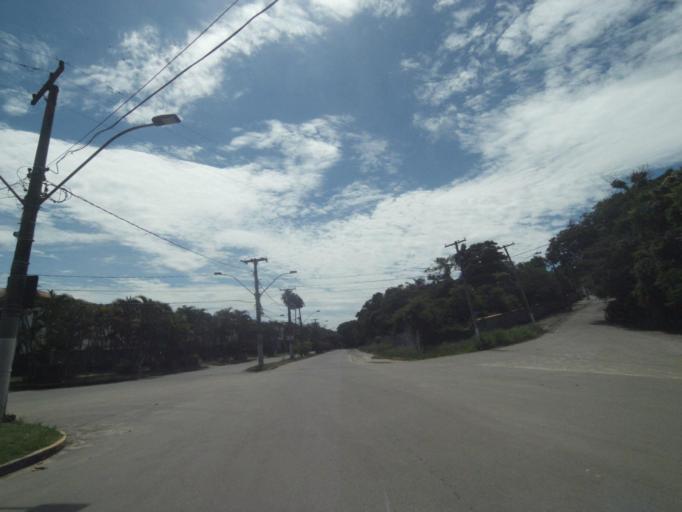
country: BR
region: Rio de Janeiro
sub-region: Niteroi
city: Niteroi
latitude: -22.9699
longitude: -43.0434
